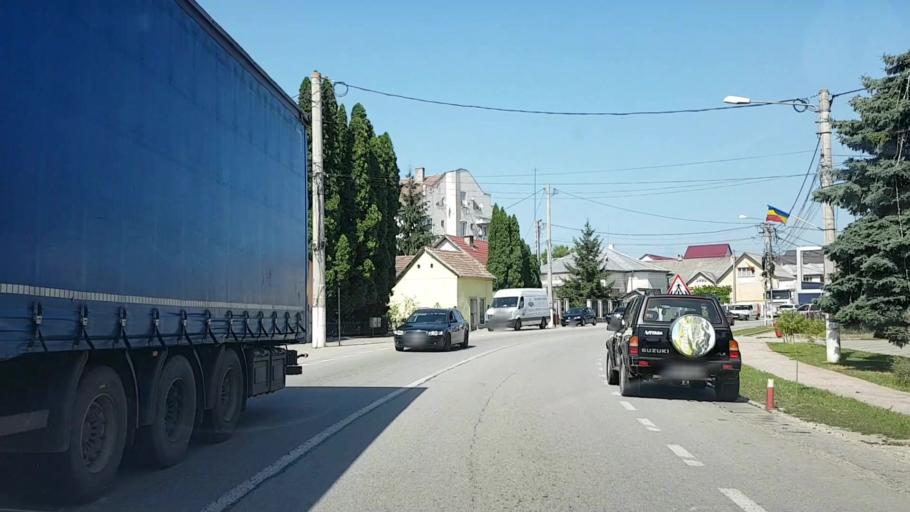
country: RO
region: Bistrita-Nasaud
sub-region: Comuna Beclean
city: Beclean
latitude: 47.1818
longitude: 24.1821
